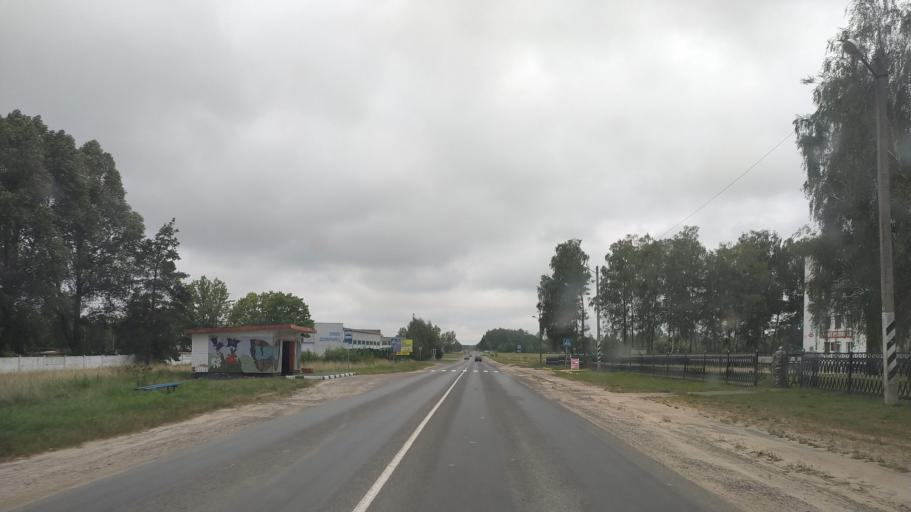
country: BY
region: Brest
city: Byaroza
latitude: 52.5512
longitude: 24.9374
